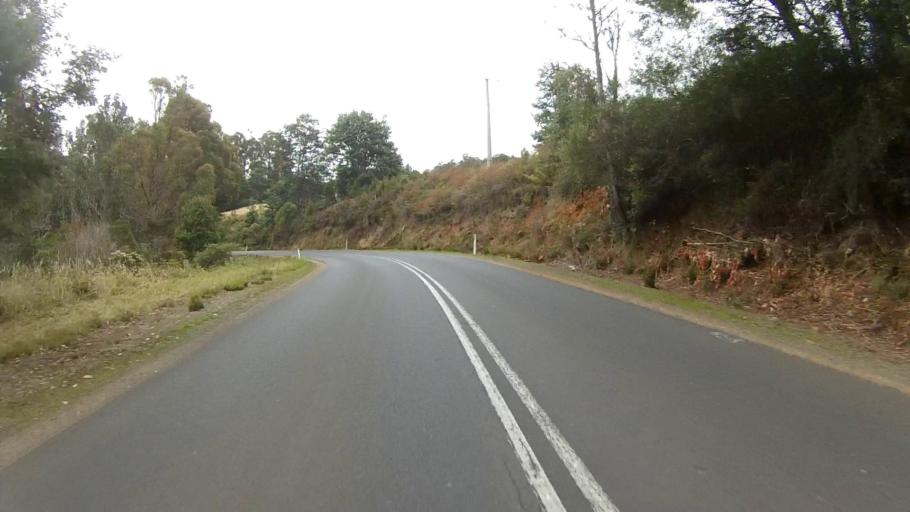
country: AU
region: Tasmania
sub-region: Huon Valley
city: Cygnet
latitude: -43.1466
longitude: 147.1534
